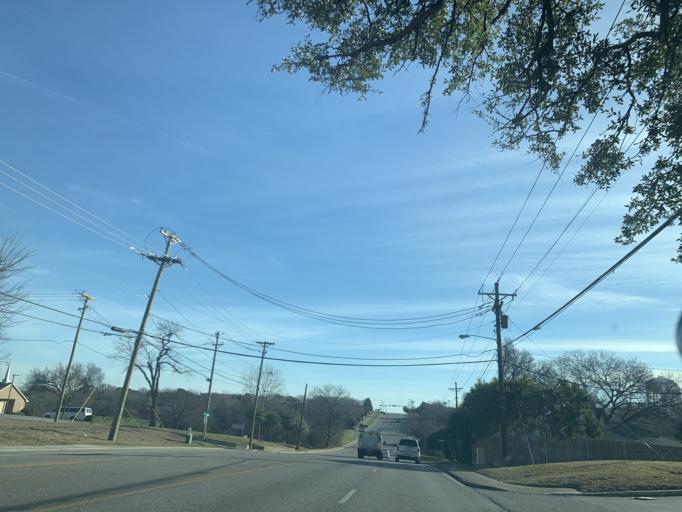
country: US
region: Texas
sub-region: Dallas County
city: DeSoto
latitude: 32.5896
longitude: -96.8507
